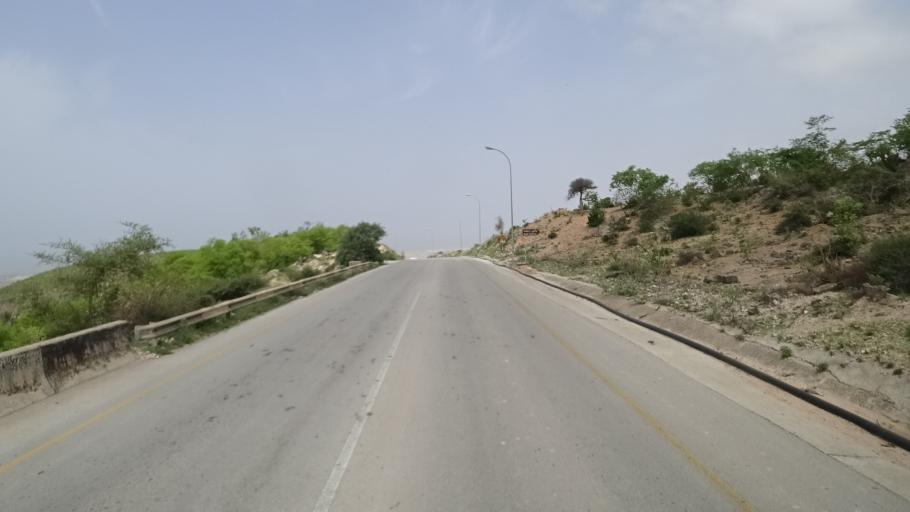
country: OM
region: Zufar
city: Salalah
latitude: 17.0721
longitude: 54.4481
